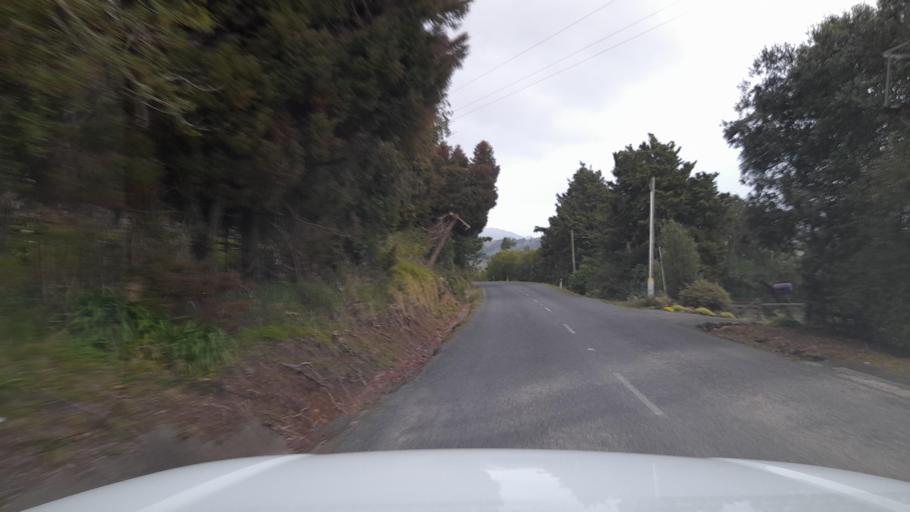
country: NZ
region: Northland
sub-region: Whangarei
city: Maungatapere
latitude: -35.6391
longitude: 174.2123
